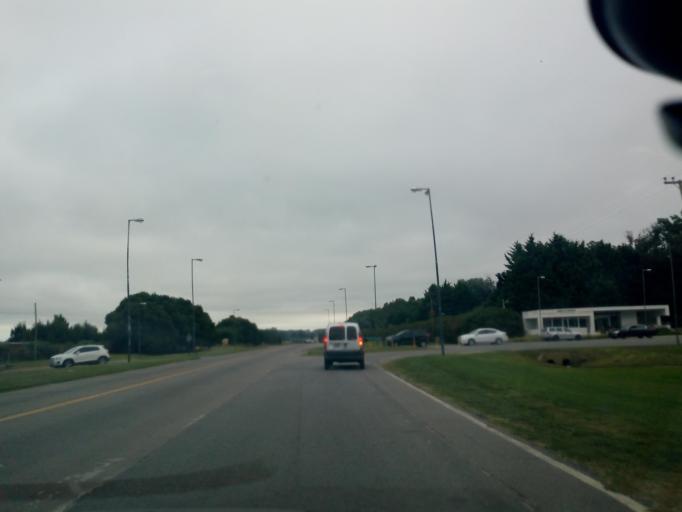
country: AR
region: Buenos Aires
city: Mar del Plata
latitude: -38.0797
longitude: -57.5843
